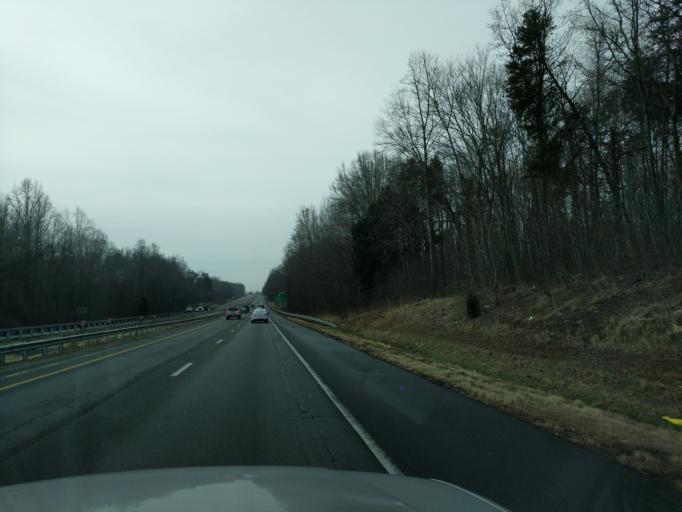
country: US
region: North Carolina
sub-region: Iredell County
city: Mooresville
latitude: 35.6094
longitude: -80.8583
